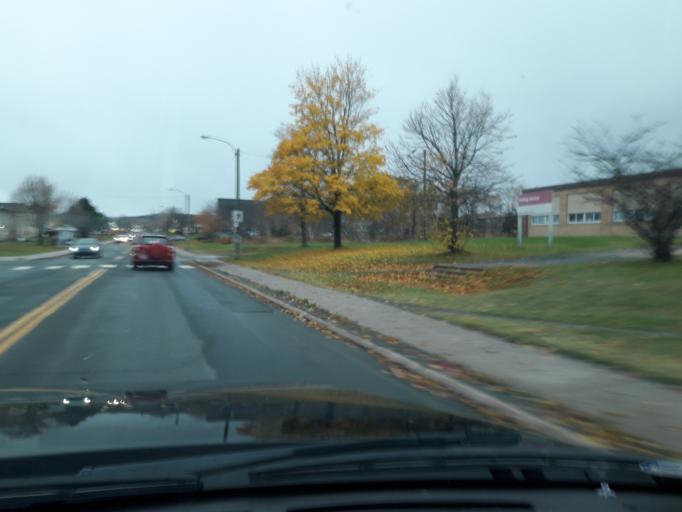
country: CA
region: Newfoundland and Labrador
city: St. John's
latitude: 47.5675
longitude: -52.7355
